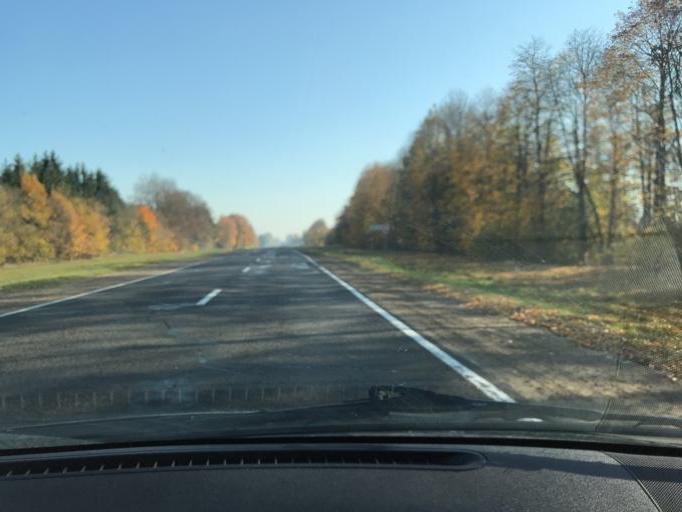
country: BY
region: Minsk
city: Klyetsk
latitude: 52.9654
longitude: 26.5270
